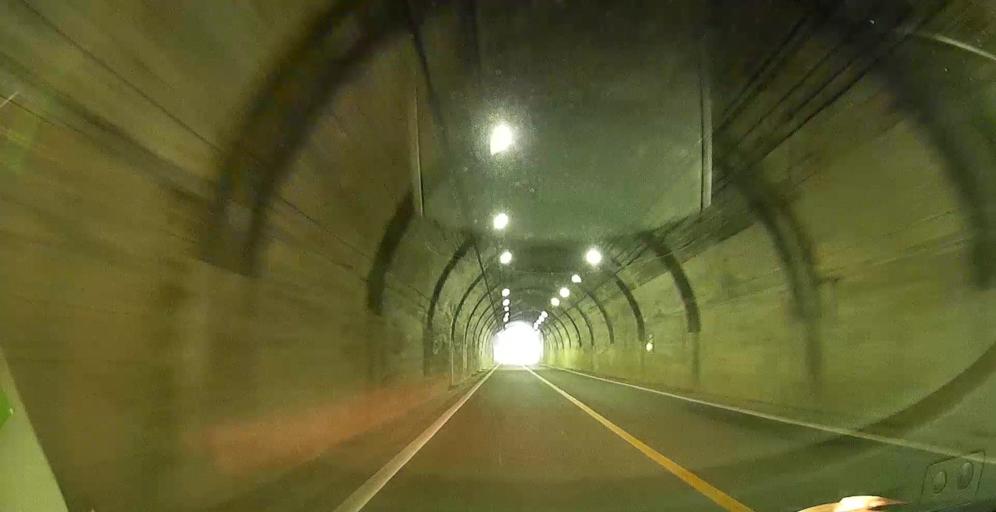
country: JP
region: Kumamoto
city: Minamata
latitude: 32.3364
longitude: 130.4879
